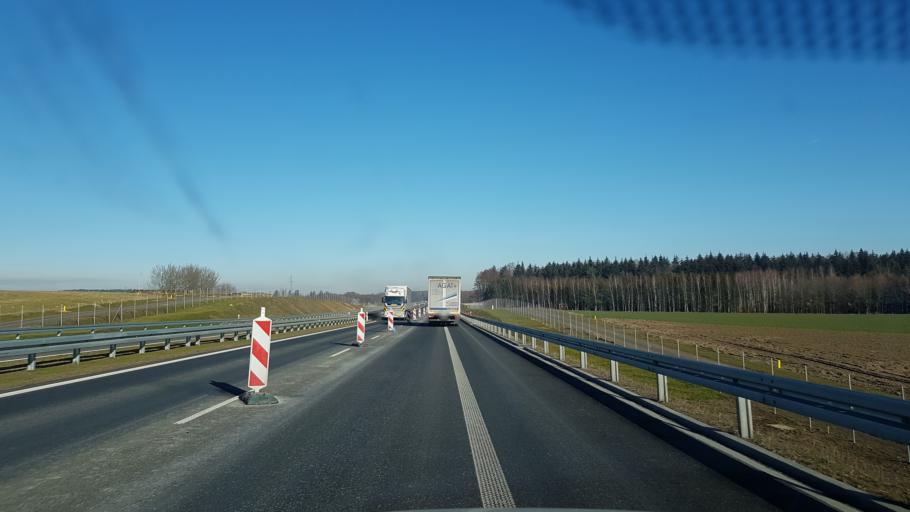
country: PL
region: West Pomeranian Voivodeship
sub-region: Powiat goleniowski
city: Przybiernow
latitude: 53.7967
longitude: 14.7769
